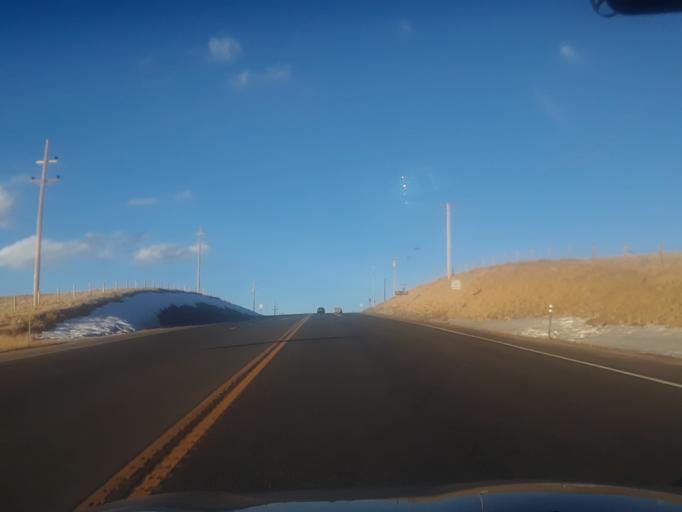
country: US
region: Colorado
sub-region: Park County
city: Fairplay
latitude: 39.3114
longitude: -105.8856
